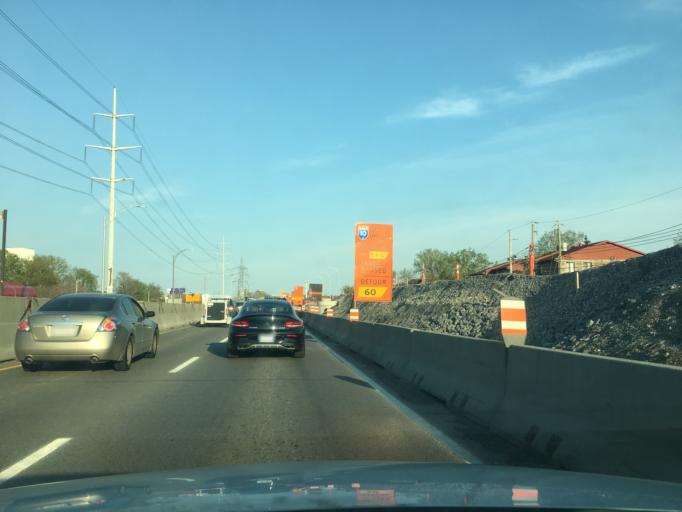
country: CA
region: Quebec
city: Westmount
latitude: 45.4738
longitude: -73.5667
